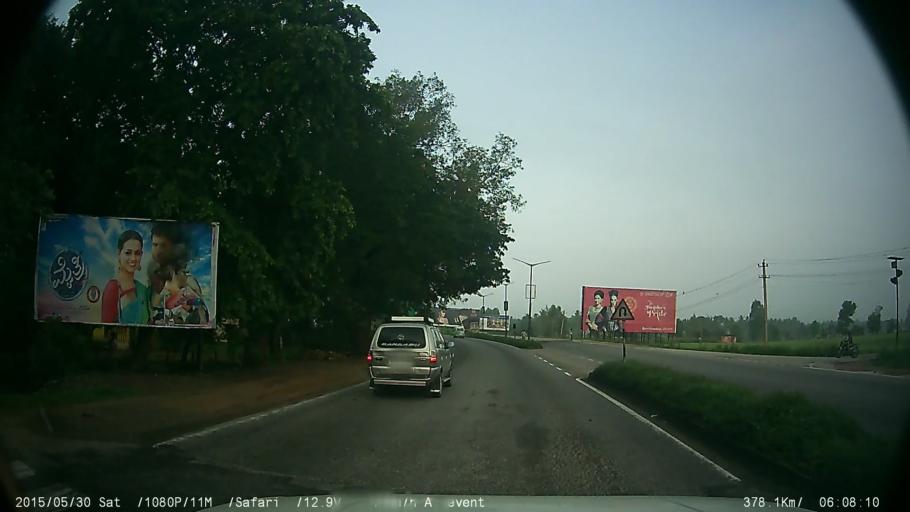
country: IN
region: Karnataka
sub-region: Mandya
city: Shrirangapattana
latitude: 12.3714
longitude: 76.6633
